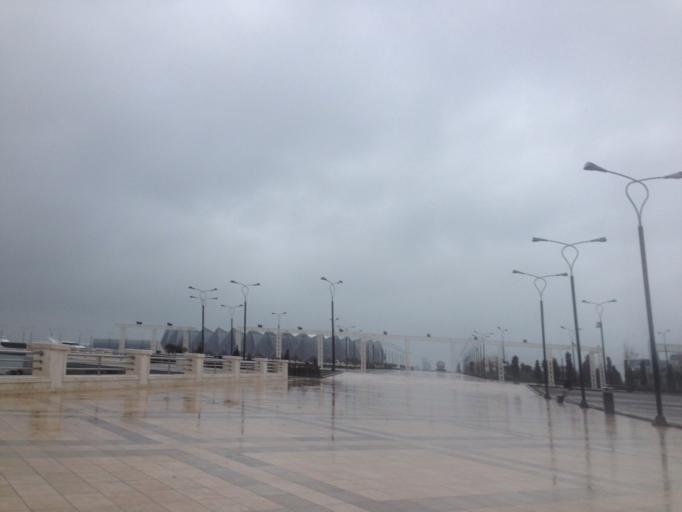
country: AZ
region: Baki
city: Badamdar
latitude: 40.3483
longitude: 49.8455
